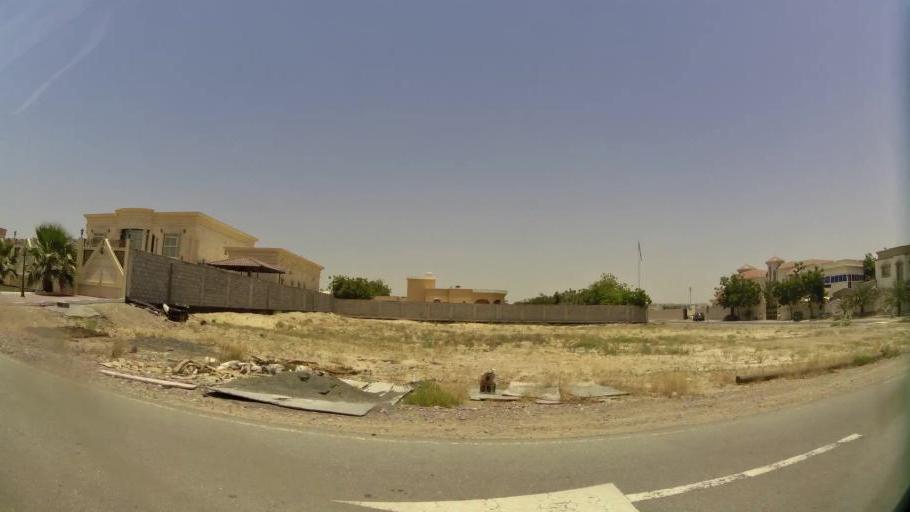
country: AE
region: Ajman
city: Ajman
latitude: 25.4085
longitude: 55.4929
